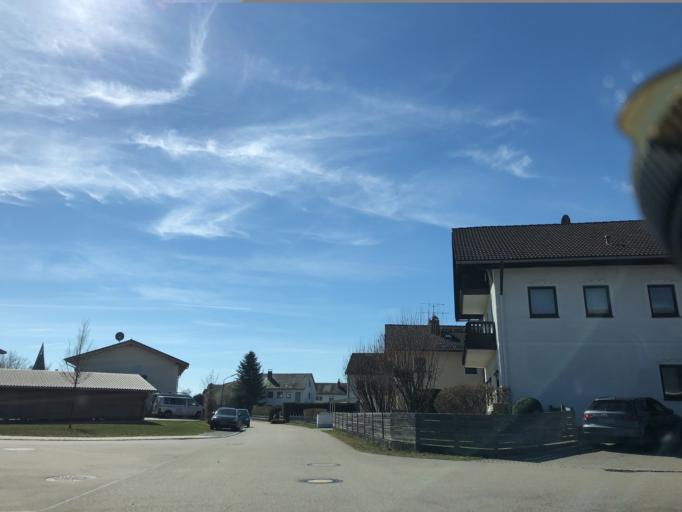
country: DE
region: Bavaria
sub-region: Upper Bavaria
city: Pfaffing
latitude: 48.0575
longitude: 12.1084
